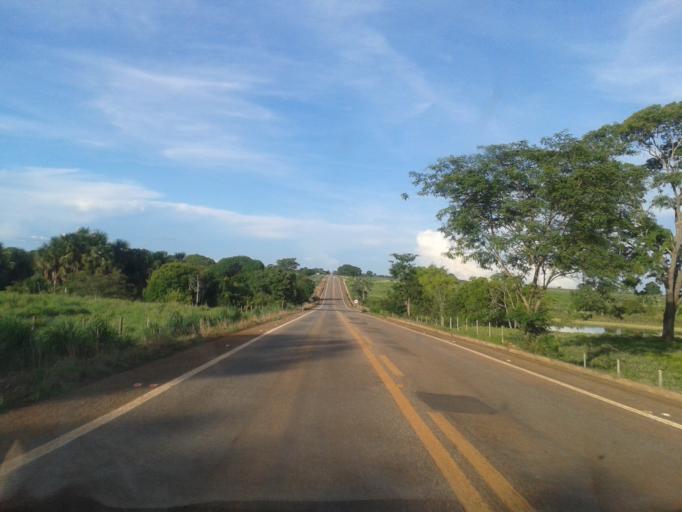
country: BR
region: Goias
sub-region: Sao Miguel Do Araguaia
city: Sao Miguel do Araguaia
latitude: -13.4398
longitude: -50.2880
